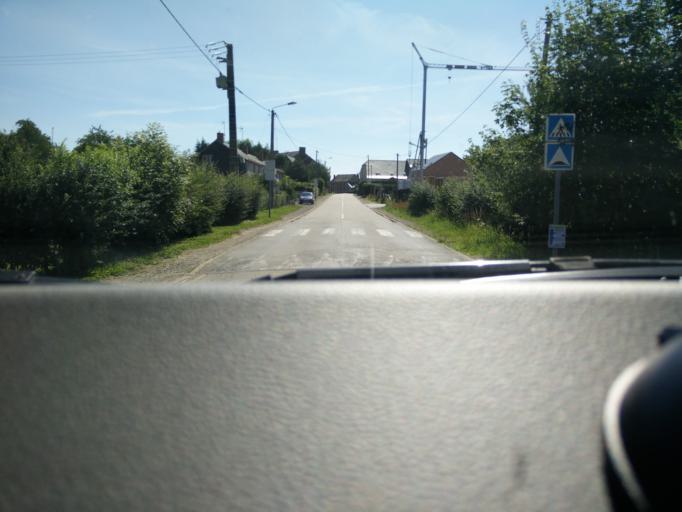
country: FR
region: Nord-Pas-de-Calais
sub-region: Departement du Nord
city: Avesnes-sur-Helpe
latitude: 50.1773
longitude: 3.9308
